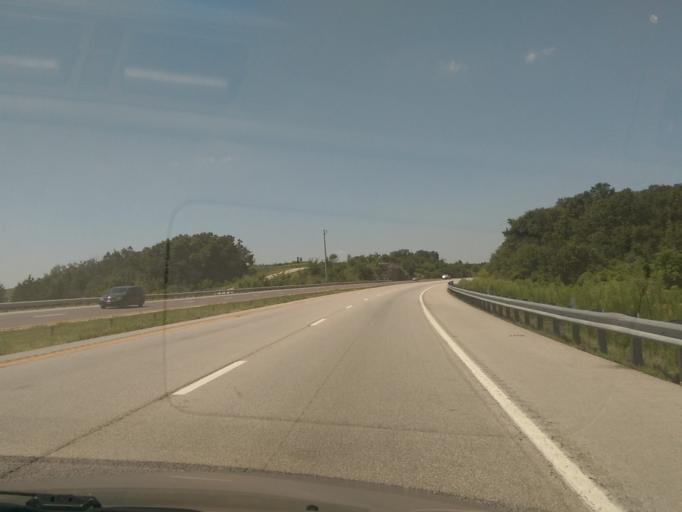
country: US
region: Missouri
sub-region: Cooper County
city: Boonville
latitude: 38.9341
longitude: -92.9760
